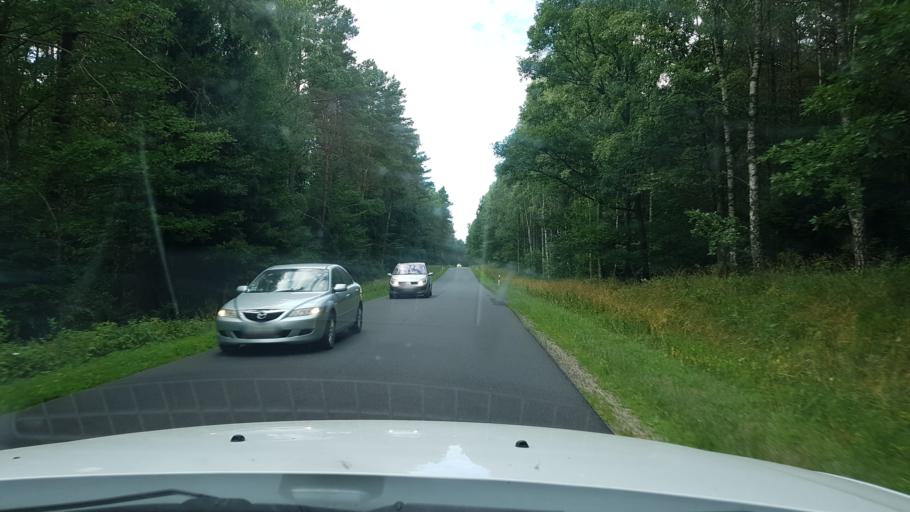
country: PL
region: West Pomeranian Voivodeship
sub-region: Powiat drawski
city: Zlocieniec
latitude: 53.5038
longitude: 16.0276
